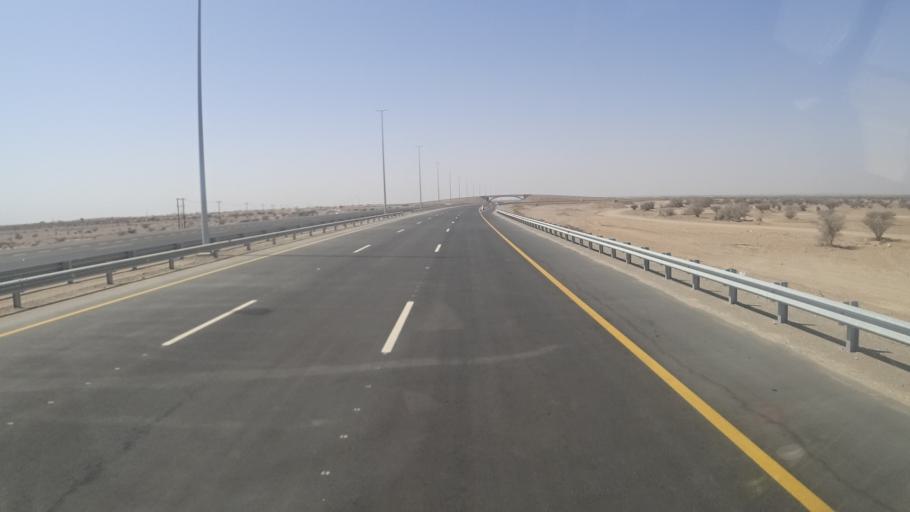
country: OM
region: Ash Sharqiyah
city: Sur
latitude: 22.2843
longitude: 59.2707
